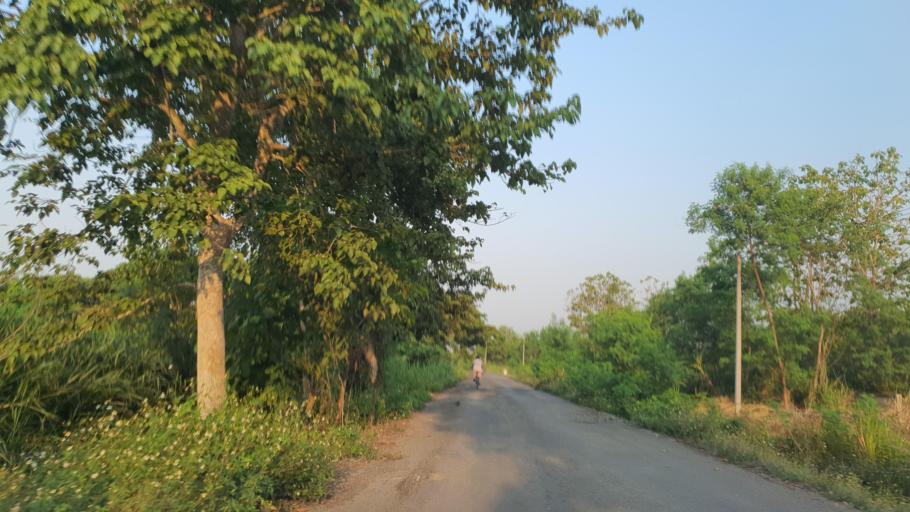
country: TH
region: Chiang Mai
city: Hang Dong
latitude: 18.6570
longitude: 98.9301
